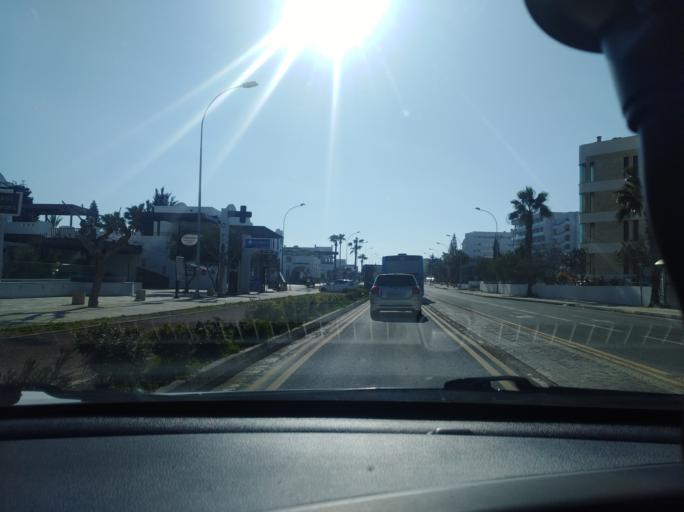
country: CY
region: Pafos
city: Paphos
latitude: 34.7438
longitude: 32.4305
